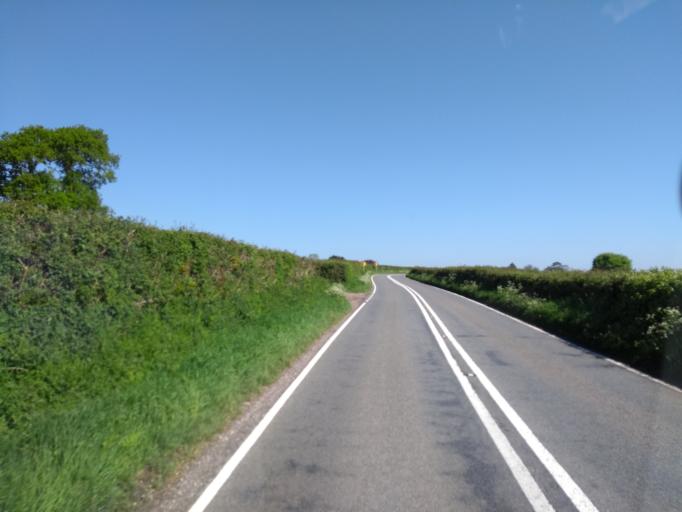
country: GB
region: England
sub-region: Somerset
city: Chard
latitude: 50.8330
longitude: -2.9627
